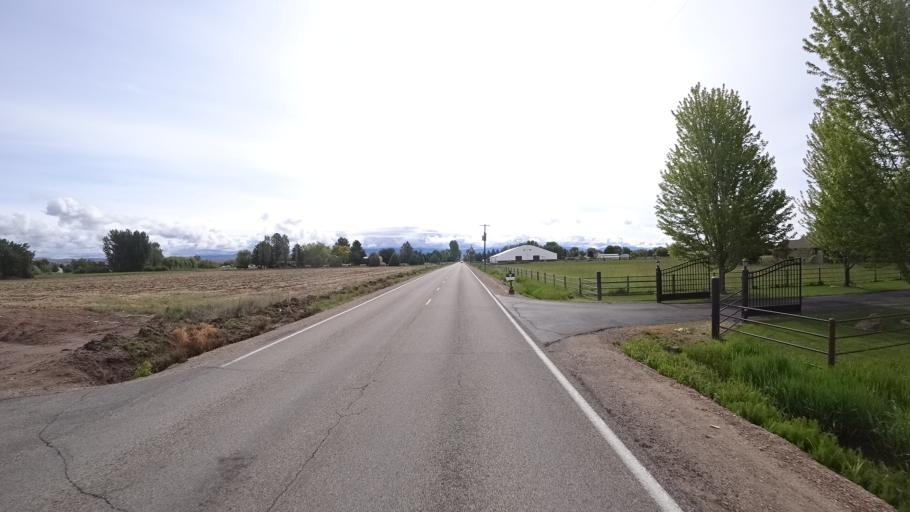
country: US
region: Idaho
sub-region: Ada County
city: Eagle
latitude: 43.7209
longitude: -116.3914
